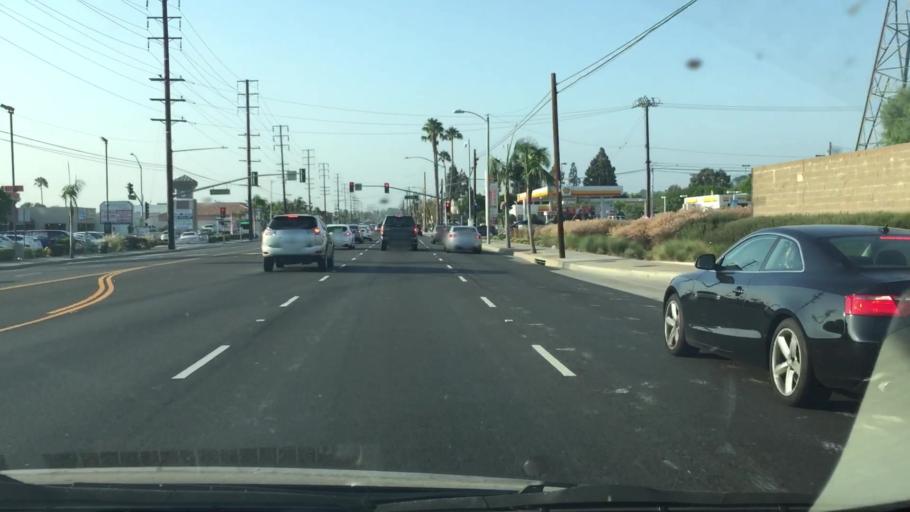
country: US
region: California
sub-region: Orange County
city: Villa Park
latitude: 33.8166
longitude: -117.8358
